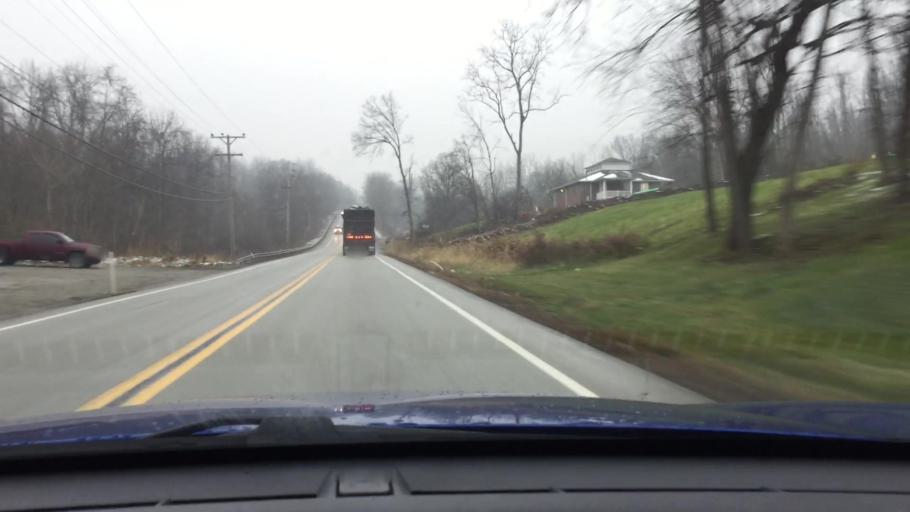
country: US
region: Pennsylvania
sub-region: Washington County
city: Canonsburg
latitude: 40.2372
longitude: -80.1728
